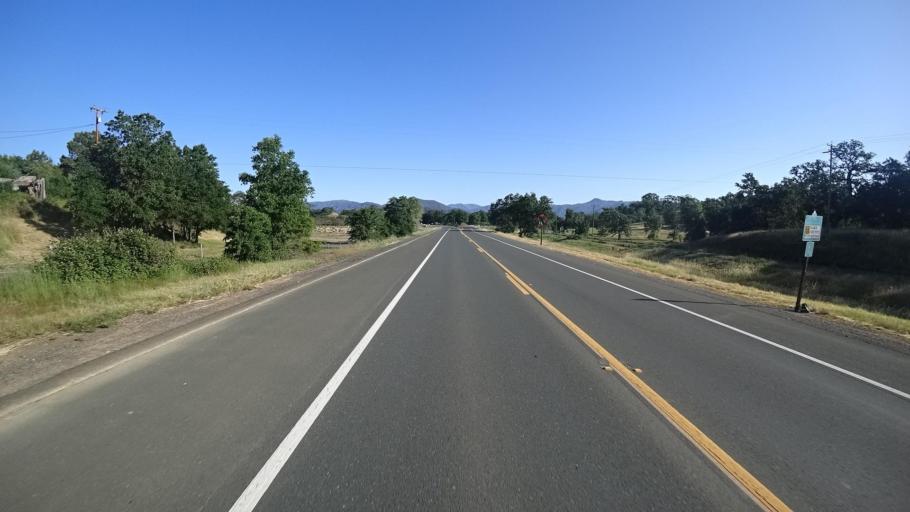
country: US
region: California
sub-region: Lake County
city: Upper Lake
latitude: 39.1355
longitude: -122.9094
